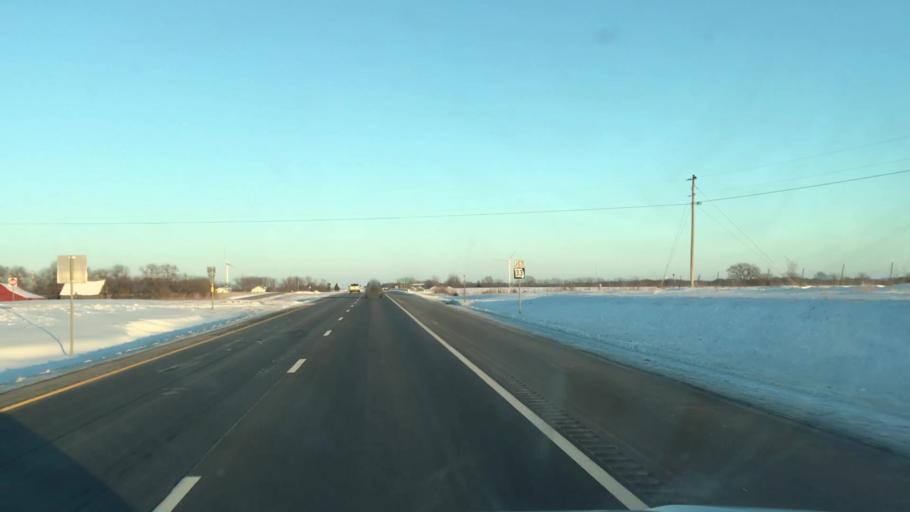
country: US
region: Missouri
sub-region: DeKalb County
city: Maysville
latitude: 39.7615
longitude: -94.4067
